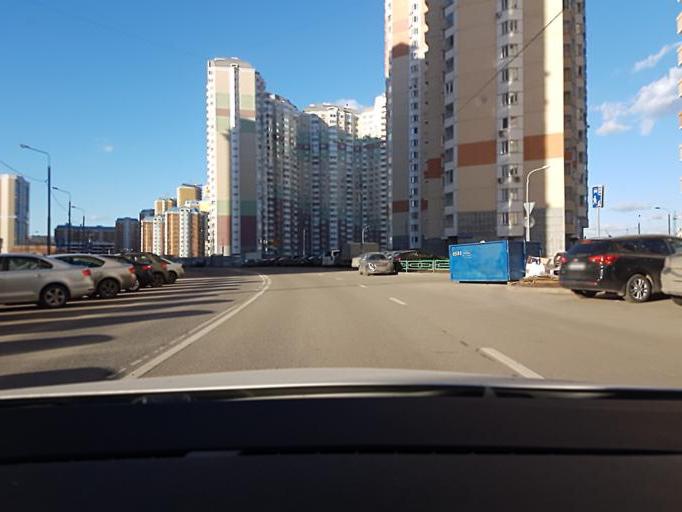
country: RU
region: Moskovskaya
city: Pavshino
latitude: 55.8219
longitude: 37.3763
